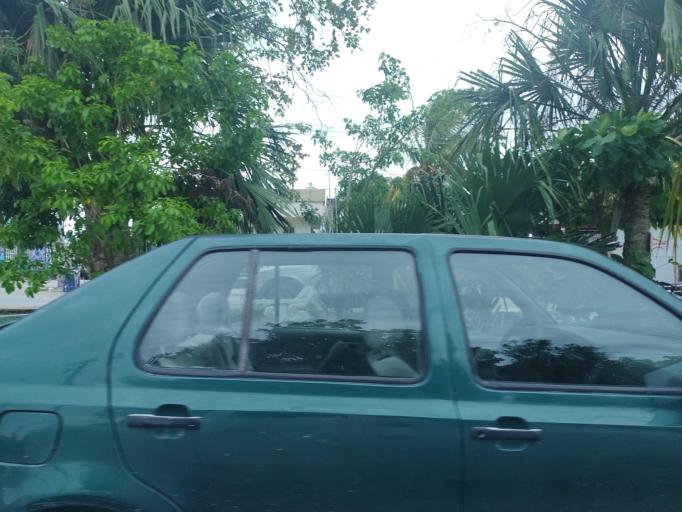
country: MX
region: Quintana Roo
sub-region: Tulum
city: Ciudad Chemuyil
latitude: 20.4016
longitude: -87.3233
